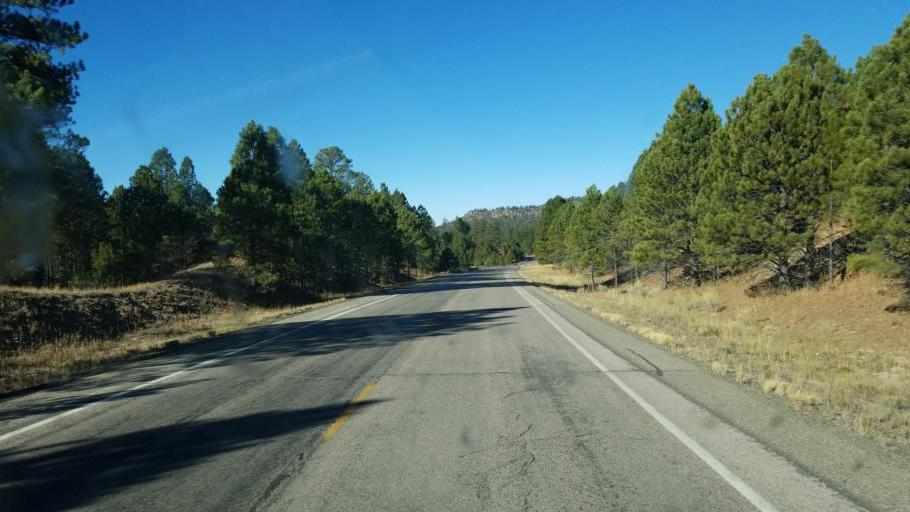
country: US
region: New Mexico
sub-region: McKinley County
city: Navajo
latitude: 36.0764
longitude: -108.9051
